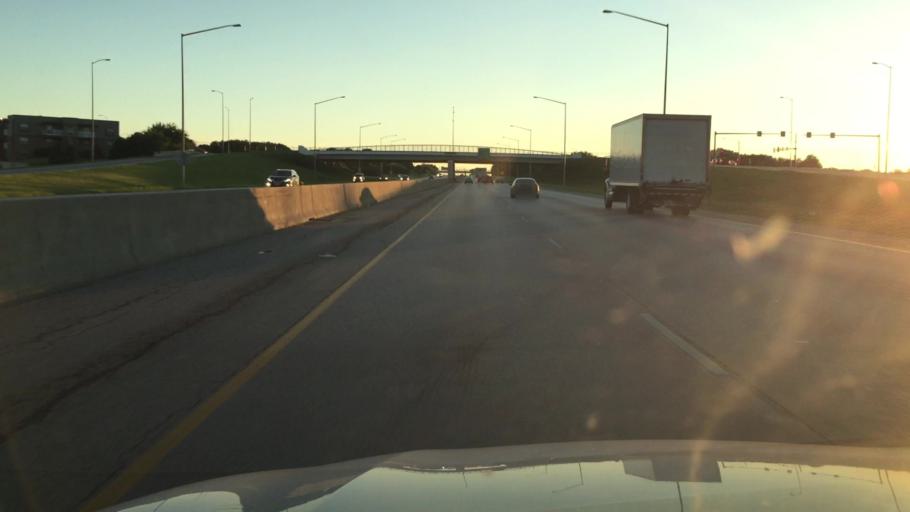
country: US
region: Iowa
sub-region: Polk County
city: Clive
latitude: 41.5924
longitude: -93.7486
